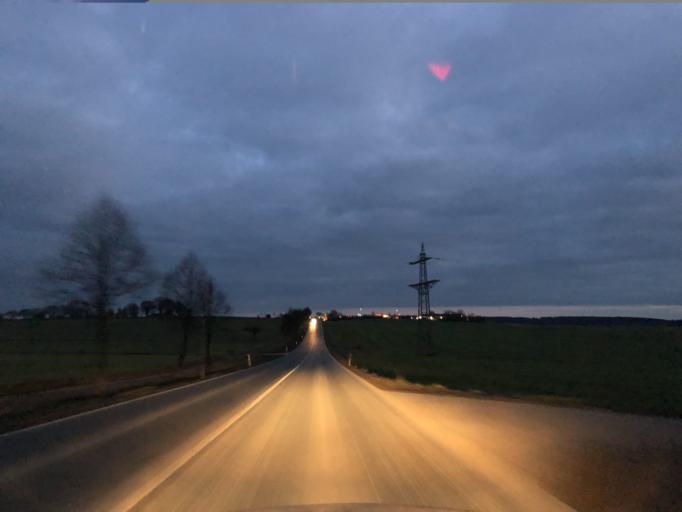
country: DE
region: Rheinland-Pfalz
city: Singhofen
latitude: 50.2863
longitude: 7.8281
